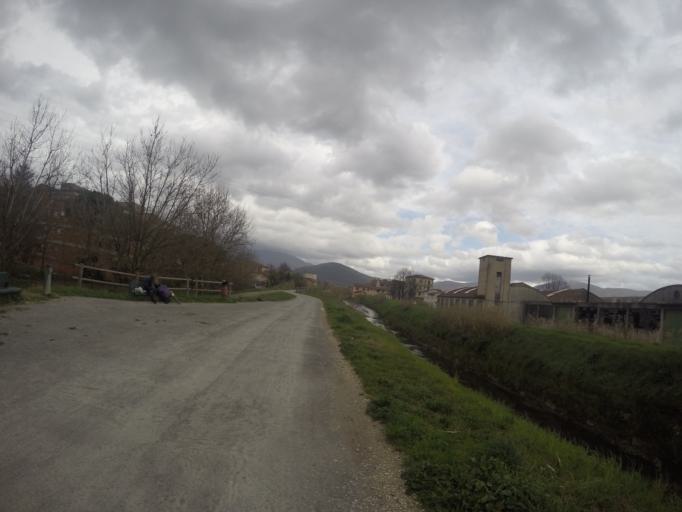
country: IT
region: Tuscany
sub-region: Provincia di Prato
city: Fornacelle
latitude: 43.8863
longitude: 11.0520
